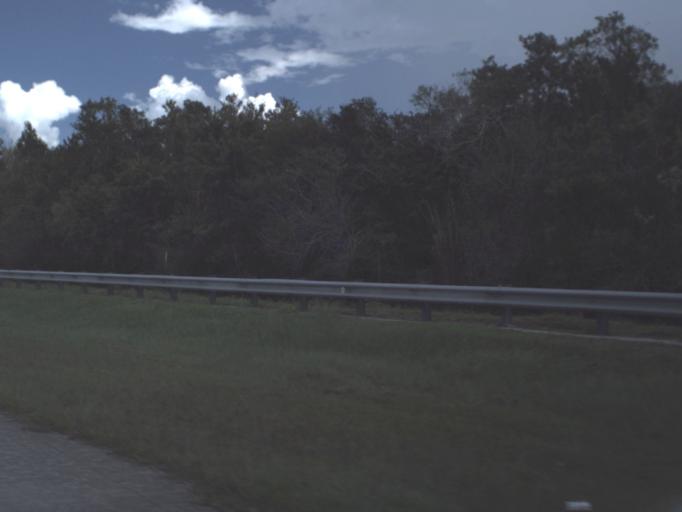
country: US
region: Florida
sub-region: Collier County
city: Orangetree
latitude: 26.0965
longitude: -81.3447
